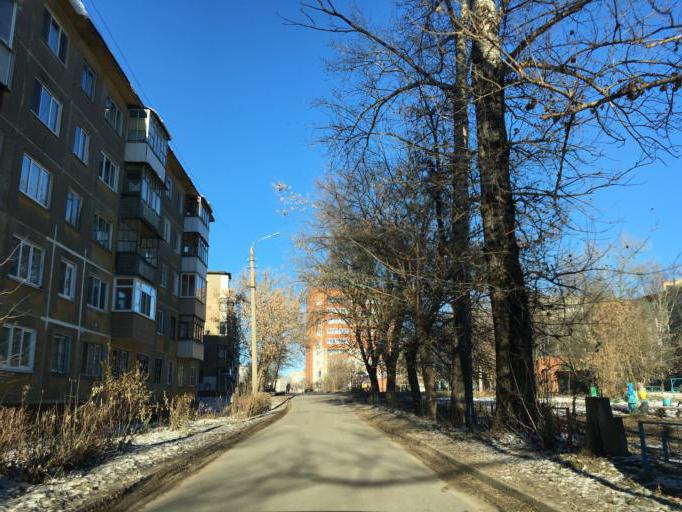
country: RU
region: Tula
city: Tula
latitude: 54.1942
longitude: 37.6769
